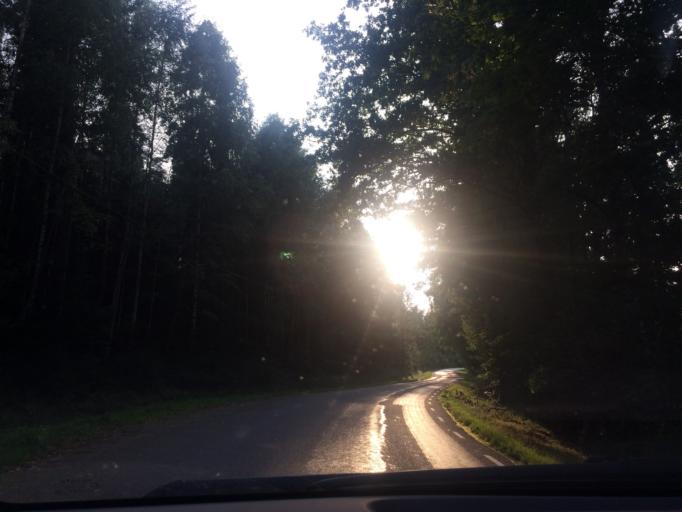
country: SE
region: Vaestra Goetaland
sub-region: Alingsas Kommun
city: Alingsas
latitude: 57.9908
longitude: 12.4647
